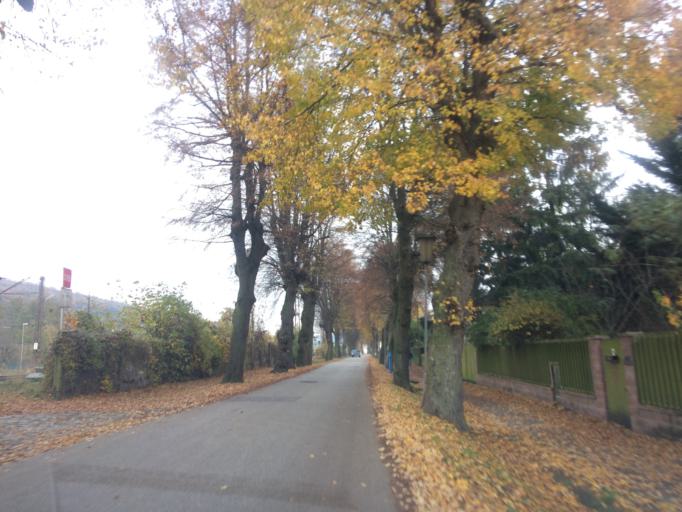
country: AT
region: Lower Austria
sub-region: Politischer Bezirk Wien-Umgebung
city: Purkersdorf
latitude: 48.2081
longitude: 16.1840
